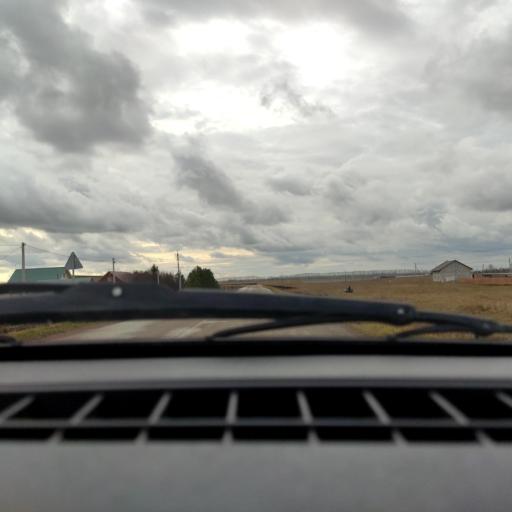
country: RU
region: Bashkortostan
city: Asanovo
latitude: 54.9611
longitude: 55.5390
